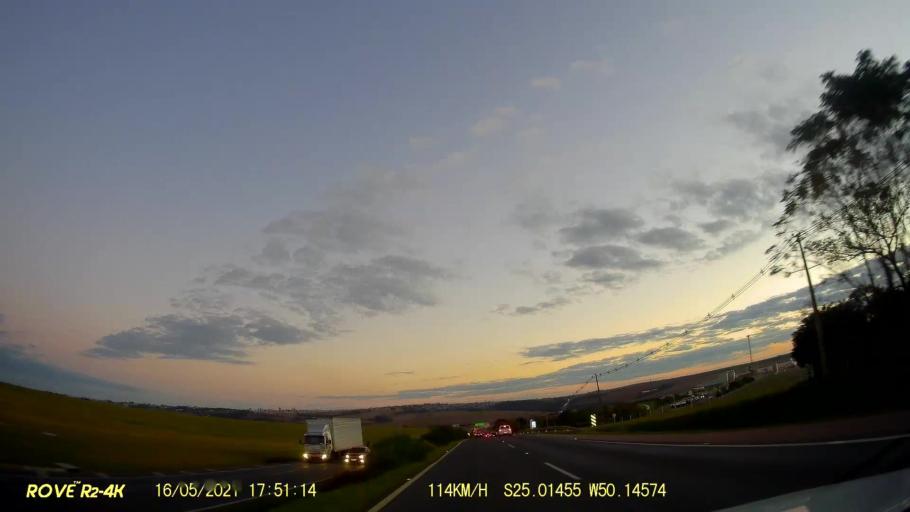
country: BR
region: Parana
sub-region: Carambei
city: Carambei
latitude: -25.0146
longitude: -50.1458
